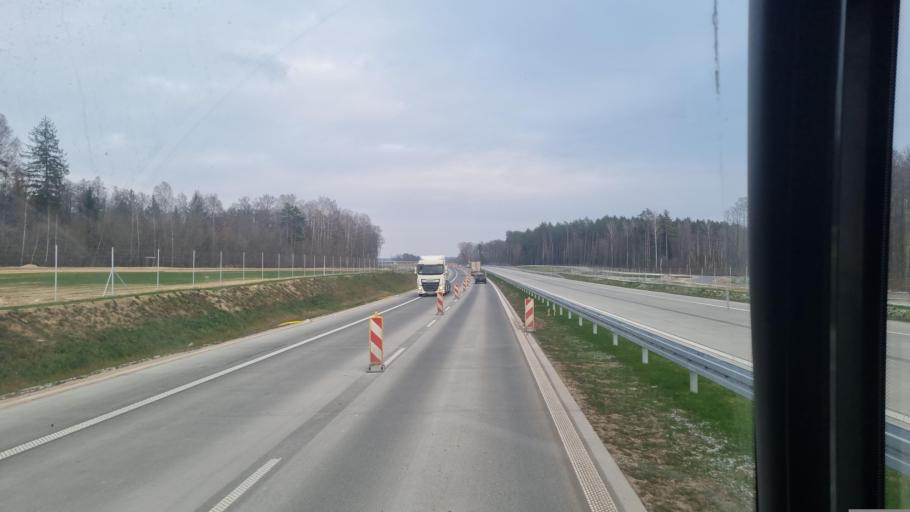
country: PL
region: Warmian-Masurian Voivodeship
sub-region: Powiat elcki
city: Elk
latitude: 53.8424
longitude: 22.4466
